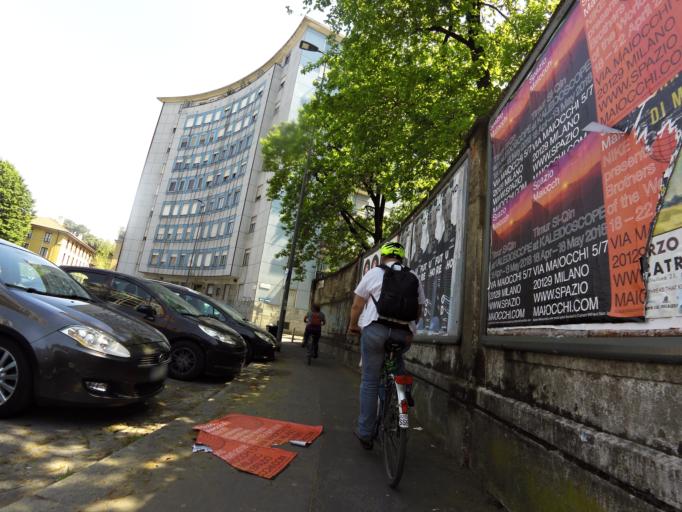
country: IT
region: Lombardy
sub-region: Citta metropolitana di Milano
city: Sesto San Giovanni
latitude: 45.4983
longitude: 9.2290
